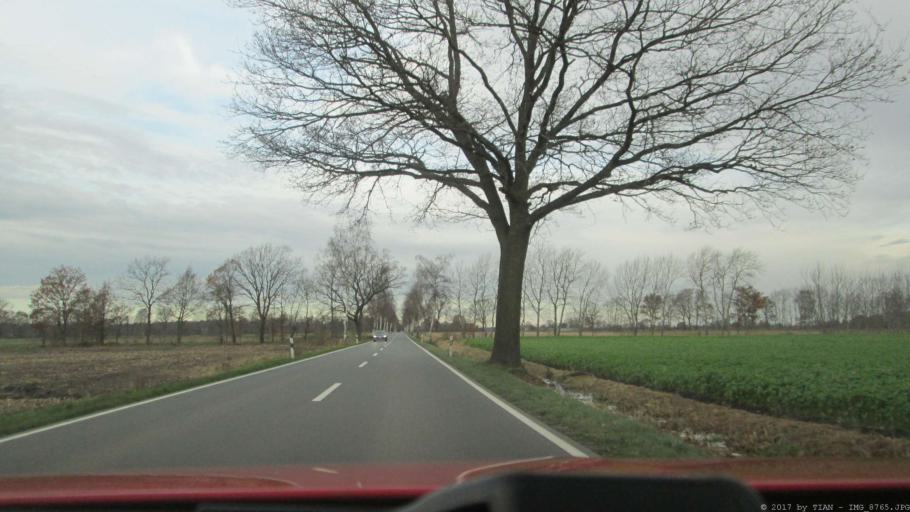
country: DE
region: Lower Saxony
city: Tiddische
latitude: 52.4876
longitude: 10.8106
